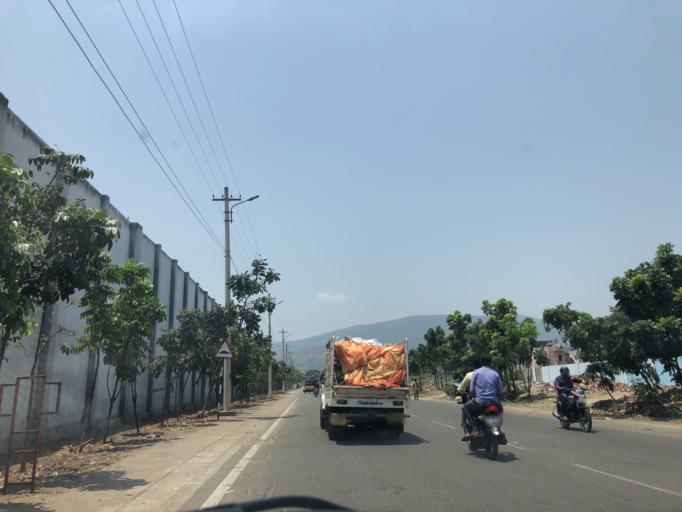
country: IN
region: Andhra Pradesh
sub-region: Vishakhapatnam
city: Yarada
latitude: 17.7139
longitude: 83.2926
